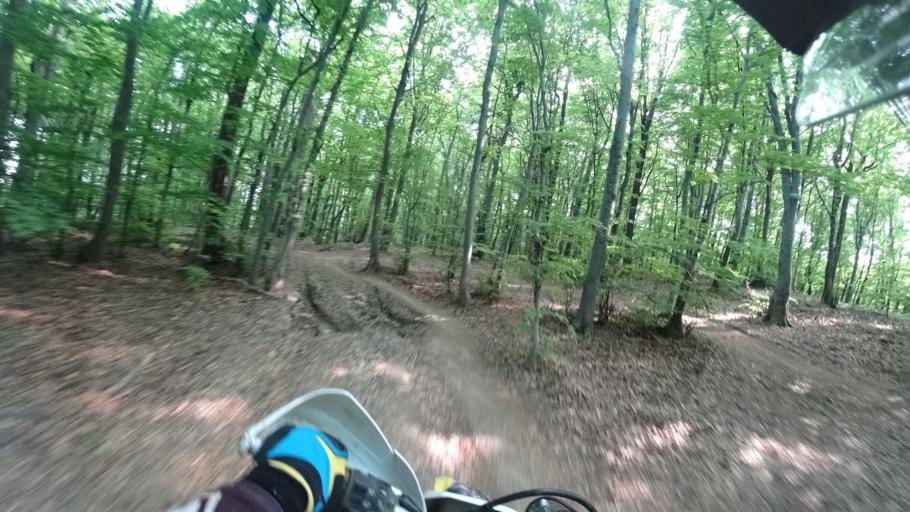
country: HR
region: Zagrebacka
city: Jablanovec
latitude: 45.8655
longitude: 15.8795
